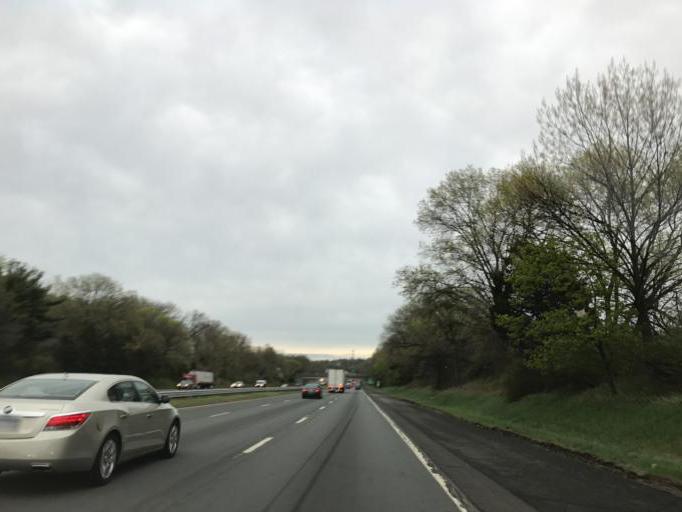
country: US
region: New Jersey
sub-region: Hunterdon County
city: Whitehouse Station
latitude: 40.6512
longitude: -74.7723
